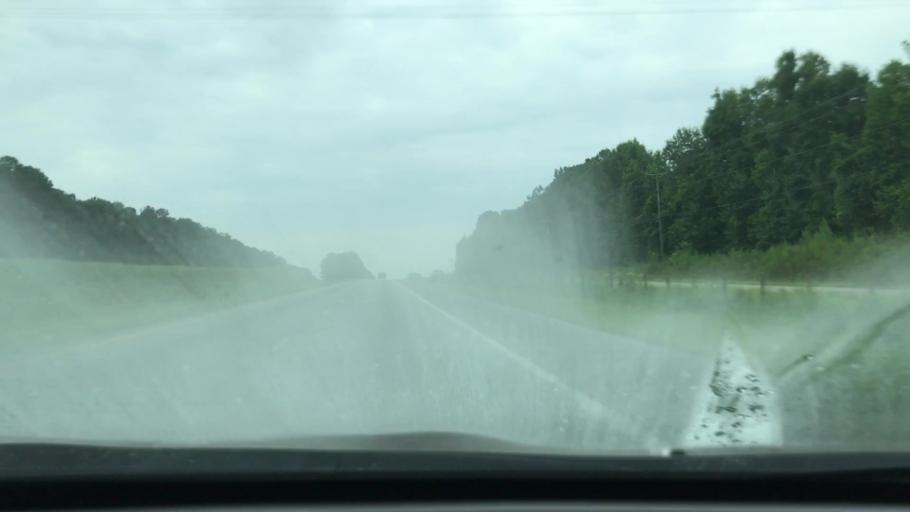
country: US
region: South Carolina
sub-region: Jasper County
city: Ridgeland
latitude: 32.5318
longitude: -80.9578
